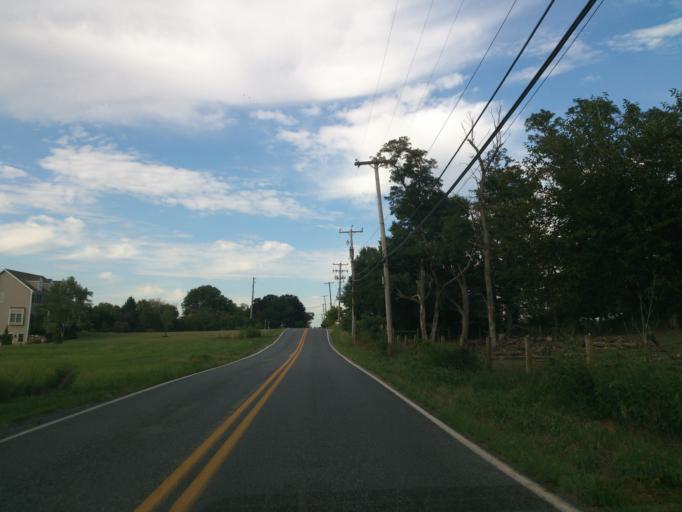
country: US
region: Pennsylvania
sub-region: Lebanon County
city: Campbelltown
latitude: 40.2434
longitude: -76.5944
